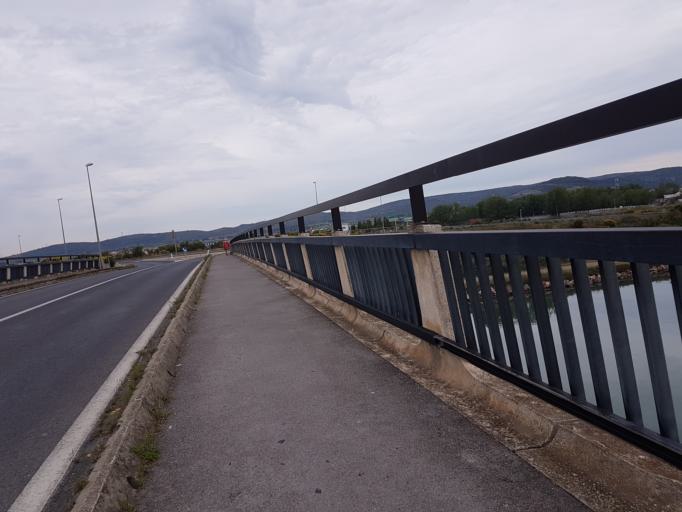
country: FR
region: Languedoc-Roussillon
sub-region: Departement de l'Herault
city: Frontignan
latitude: 43.4369
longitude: 3.7624
